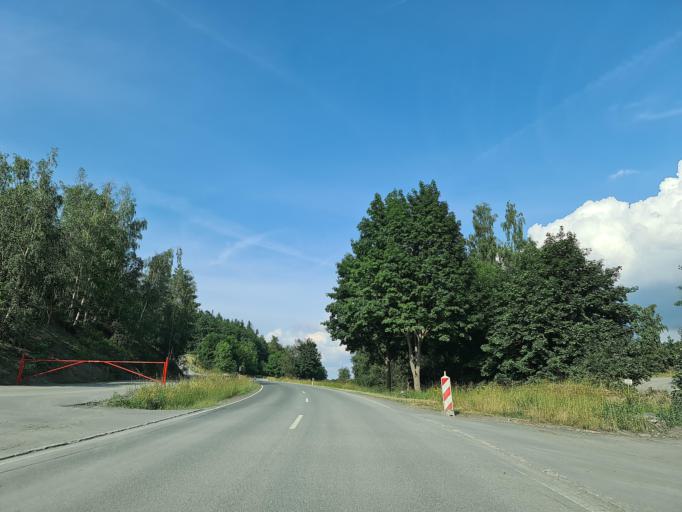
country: DE
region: Saxony
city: Bosenbrunn
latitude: 50.4011
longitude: 12.1105
